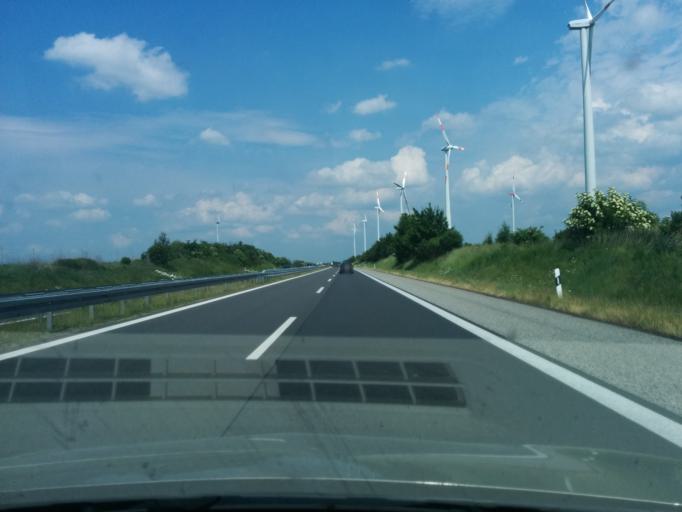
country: DE
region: Brandenburg
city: Schenkenberg
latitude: 53.3764
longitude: 13.9853
